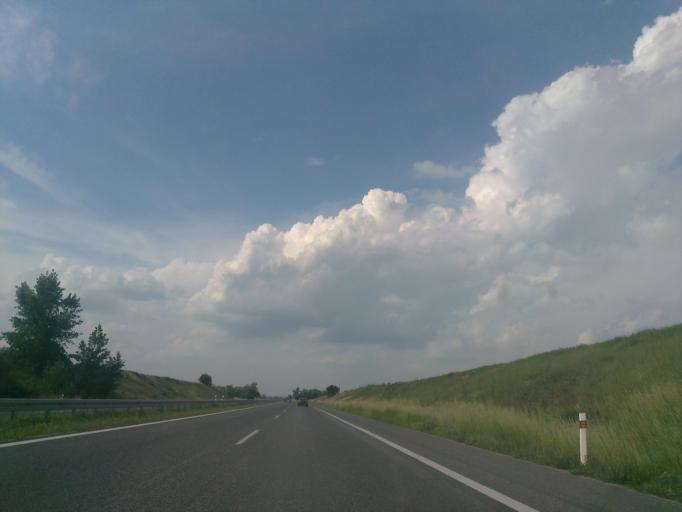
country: CZ
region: South Moravian
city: Pohorelice
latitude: 49.0113
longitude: 16.5493
